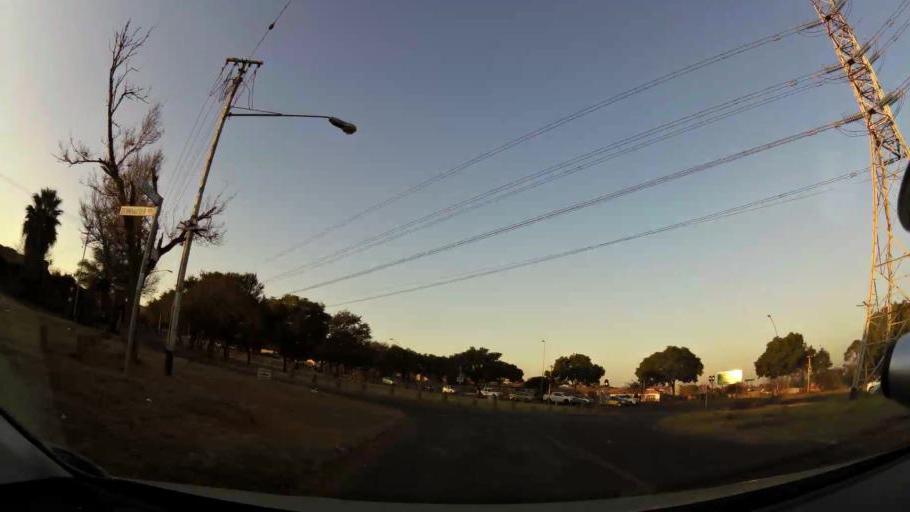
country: ZA
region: Gauteng
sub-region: City of Tshwane Metropolitan Municipality
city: Pretoria
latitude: -25.7436
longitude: 28.1343
